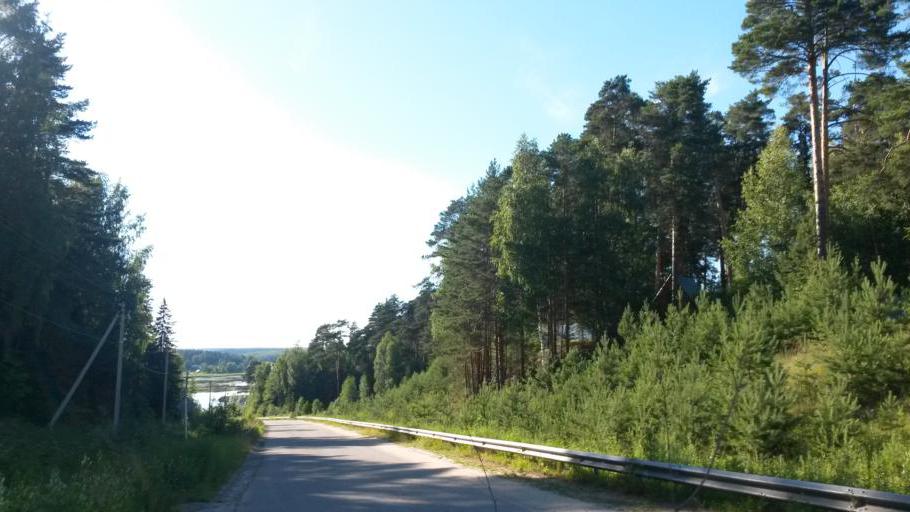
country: RU
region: Ivanovo
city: Zarechnyy
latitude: 57.5001
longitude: 42.3316
